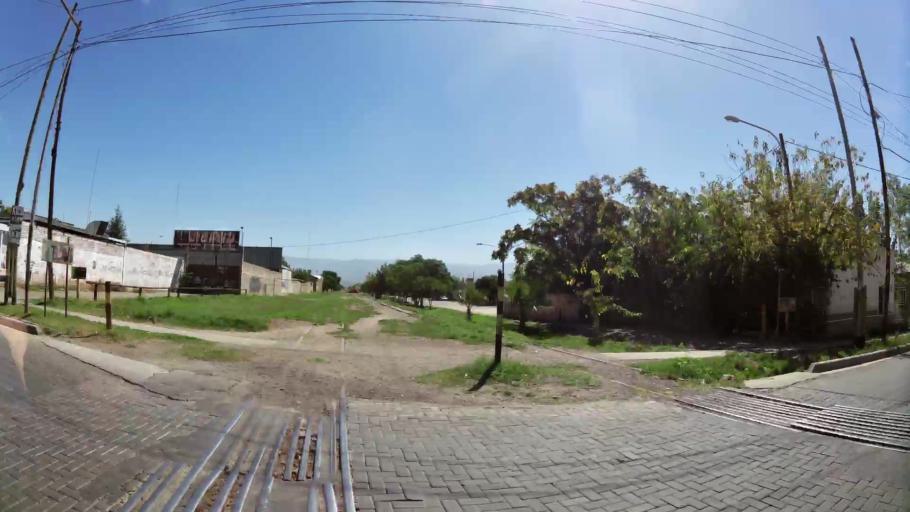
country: AR
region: Mendoza
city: Villa Nueva
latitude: -32.8930
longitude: -68.7894
